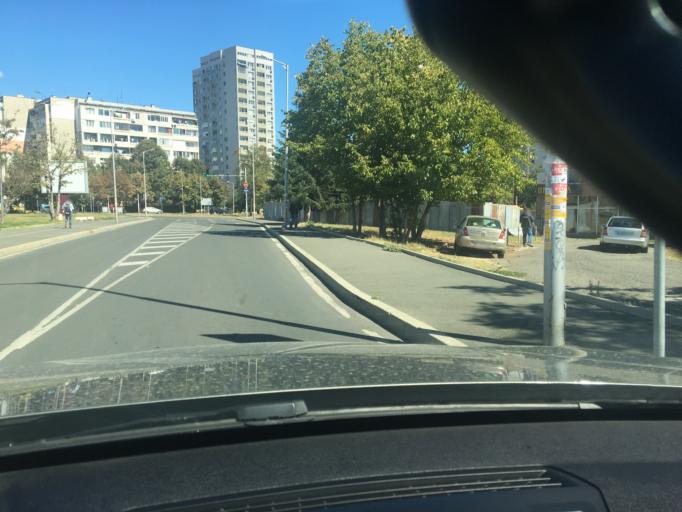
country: BG
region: Burgas
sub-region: Obshtina Burgas
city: Burgas
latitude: 42.5257
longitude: 27.4647
